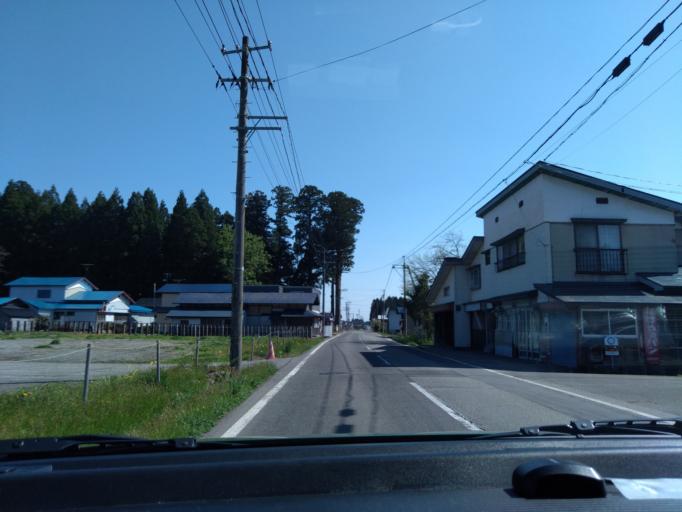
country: JP
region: Akita
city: Kakunodatemachi
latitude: 39.5514
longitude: 140.5860
